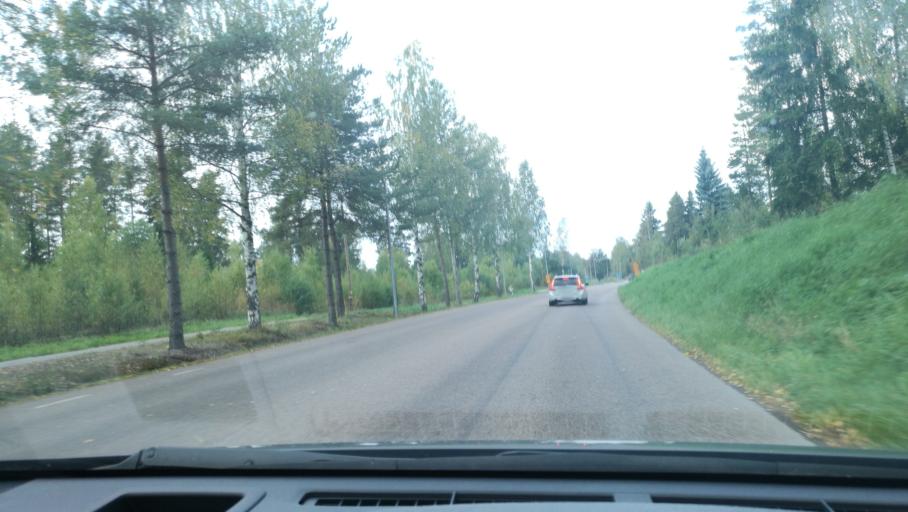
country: SE
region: Dalarna
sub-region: Avesta Kommun
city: Avesta
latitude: 60.1580
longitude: 16.1962
